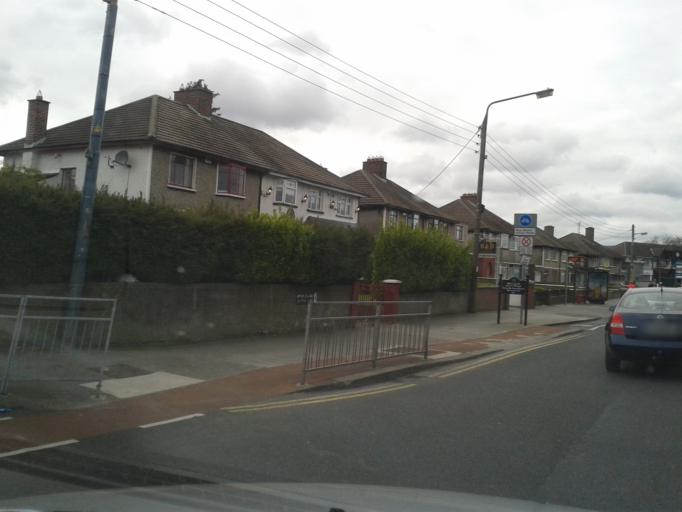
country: IE
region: Leinster
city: Beaumont
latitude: 53.3877
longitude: -6.2444
